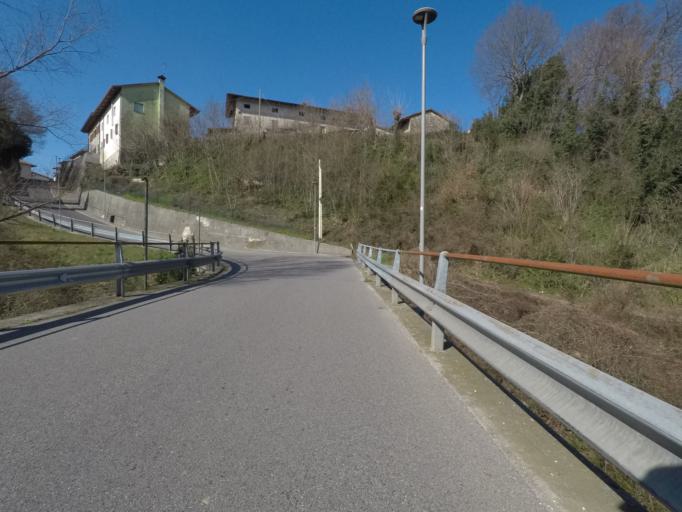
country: IT
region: Friuli Venezia Giulia
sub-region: Provincia di Udine
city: Orsaria
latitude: 46.0379
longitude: 13.3848
